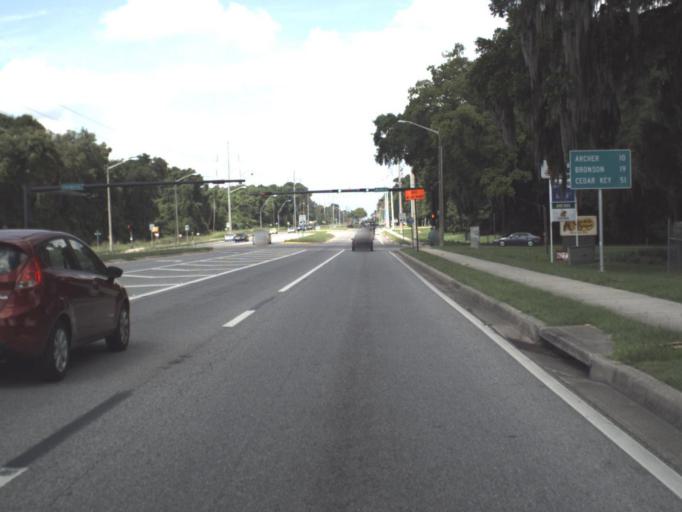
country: US
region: Florida
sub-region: Alachua County
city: Gainesville
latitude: 29.6163
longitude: -82.3883
